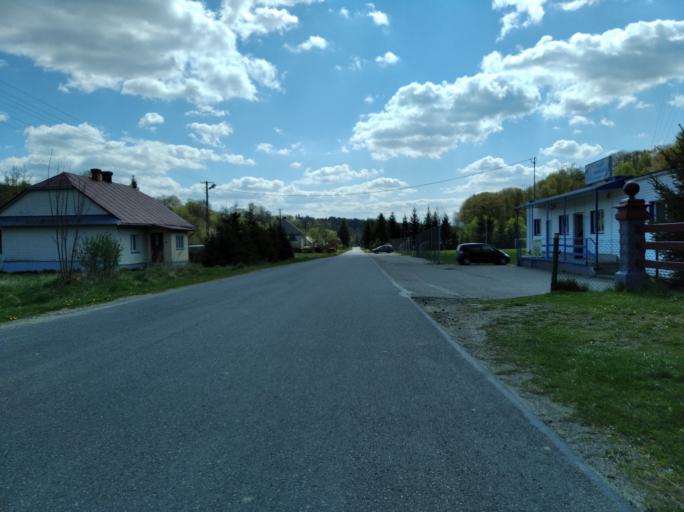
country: PL
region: Subcarpathian Voivodeship
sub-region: Powiat brzozowski
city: Wesola
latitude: 49.7979
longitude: 22.1027
